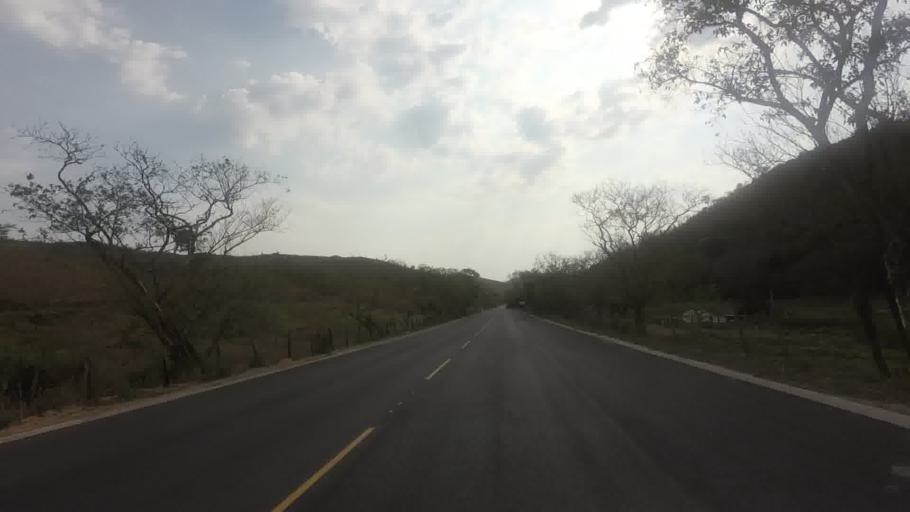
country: BR
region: Rio de Janeiro
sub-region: Itaperuna
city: Itaperuna
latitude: -21.2922
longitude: -41.8133
